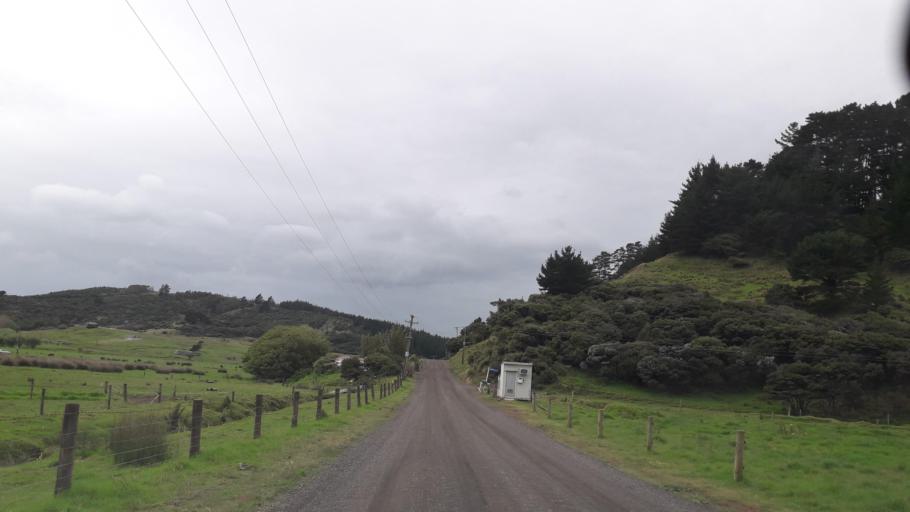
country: NZ
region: Northland
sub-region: Far North District
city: Ahipara
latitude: -35.4410
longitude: 173.3210
